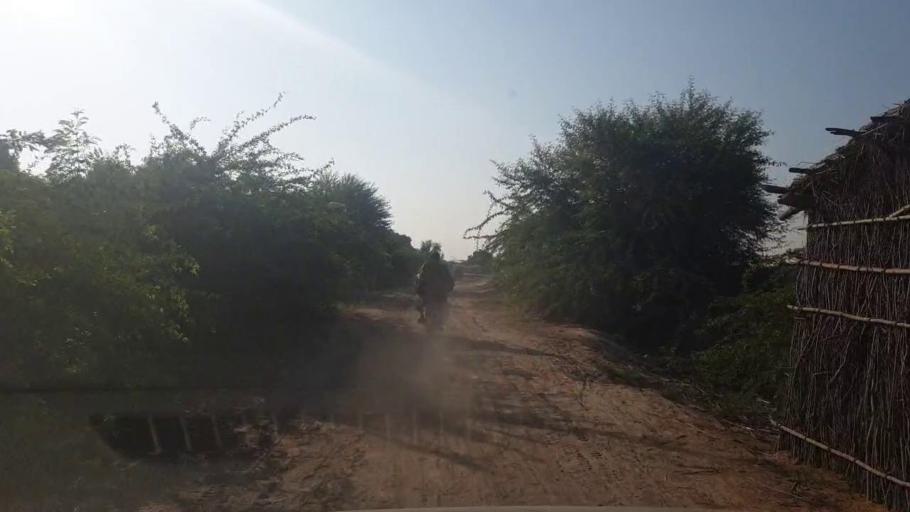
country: PK
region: Sindh
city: Tando Bago
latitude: 24.7341
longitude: 68.9315
